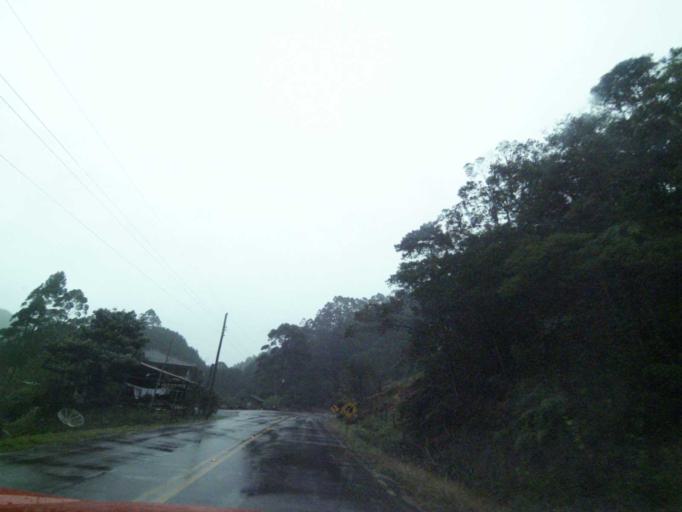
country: BR
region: Santa Catarina
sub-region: Anitapolis
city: Anitapolis
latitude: -27.7886
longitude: -49.0435
